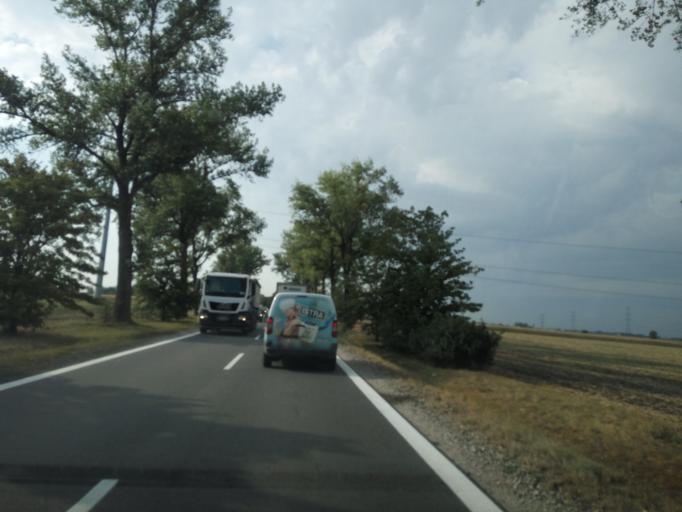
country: PL
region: Lower Silesian Voivodeship
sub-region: Powiat wroclawski
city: Zerniki Wroclawskie
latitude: 51.0083
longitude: 17.0645
